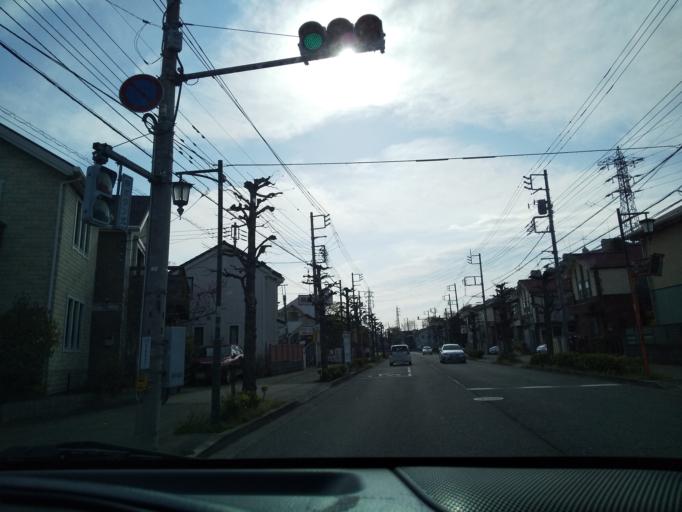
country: JP
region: Tokyo
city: Hino
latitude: 35.6907
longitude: 139.4298
